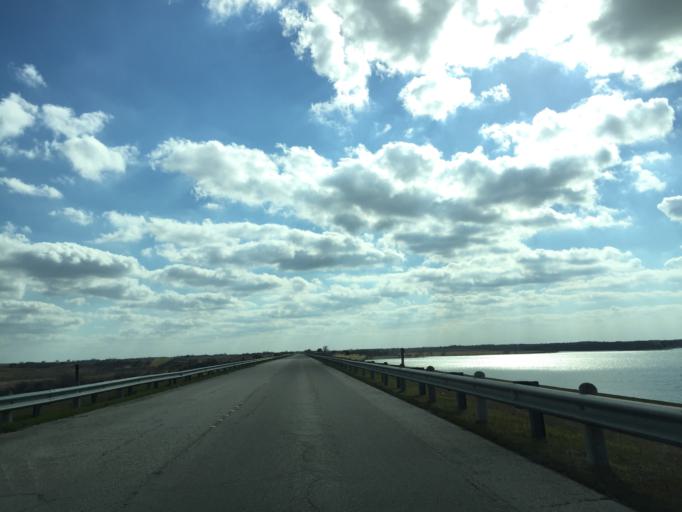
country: US
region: Texas
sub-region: Williamson County
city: Granger
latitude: 30.6950
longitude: -97.3331
